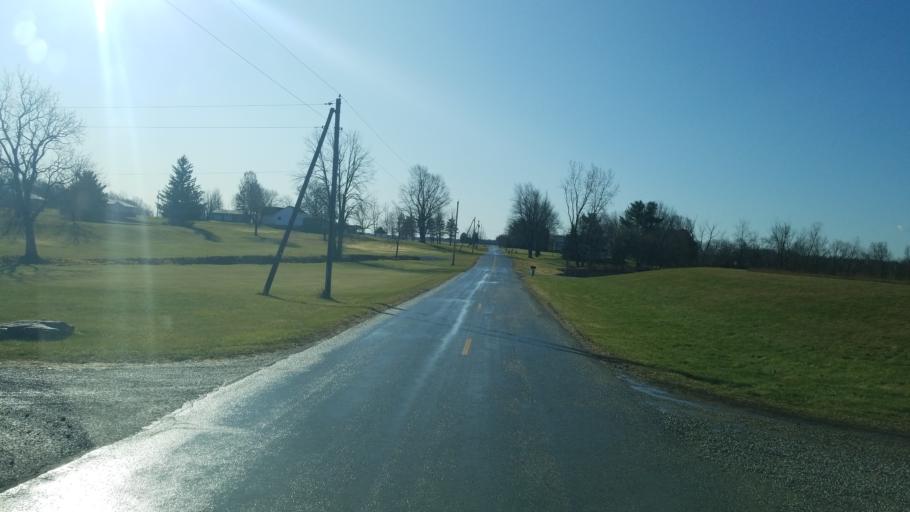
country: US
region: Ohio
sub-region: Richland County
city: Shelby
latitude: 40.8419
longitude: -82.6775
